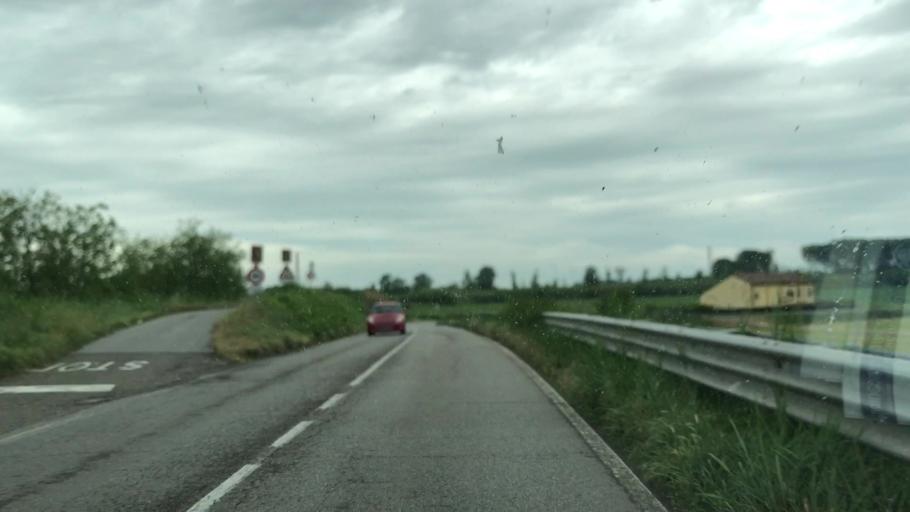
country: IT
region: Lombardy
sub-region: Provincia di Mantova
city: Quistello
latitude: 45.0076
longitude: 10.9750
